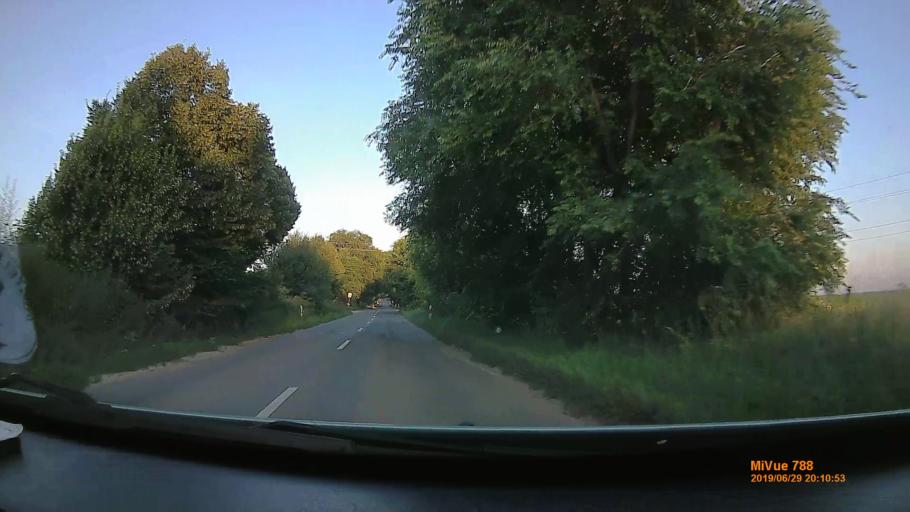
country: HU
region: Pest
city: Paty
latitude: 47.5317
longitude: 18.7829
